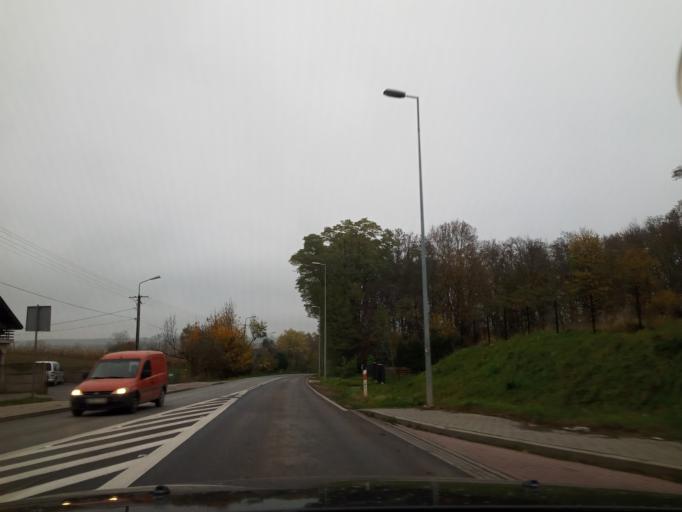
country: PL
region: Lesser Poland Voivodeship
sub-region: Powiat proszowicki
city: Klimontow
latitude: 50.2214
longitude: 20.3155
